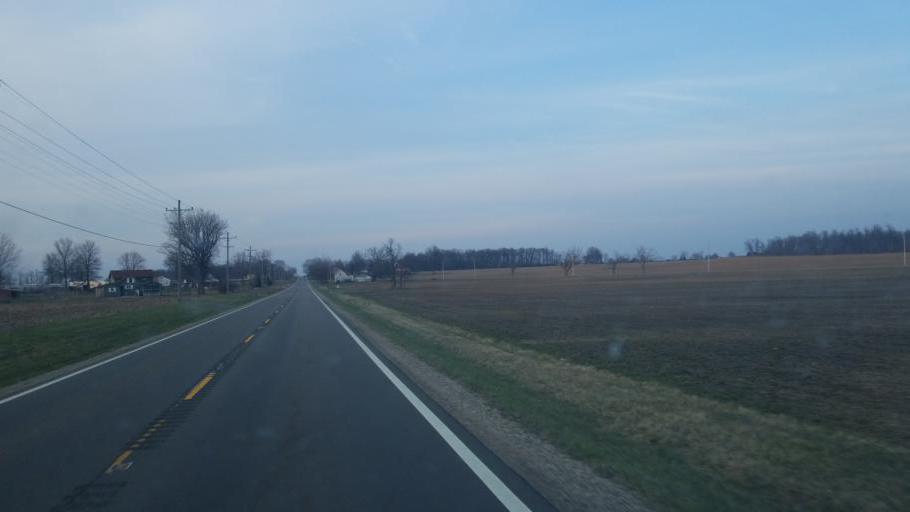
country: US
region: Ohio
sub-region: Marion County
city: Prospect
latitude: 40.5026
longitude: -83.1784
